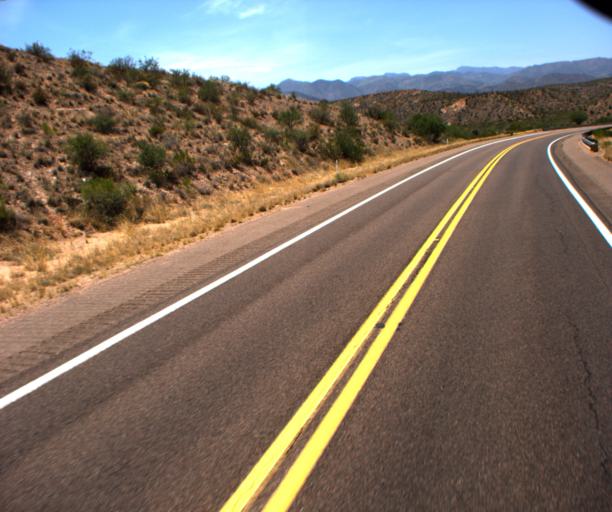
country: US
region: Arizona
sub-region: Gila County
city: Tonto Basin
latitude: 33.9192
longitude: -111.3169
